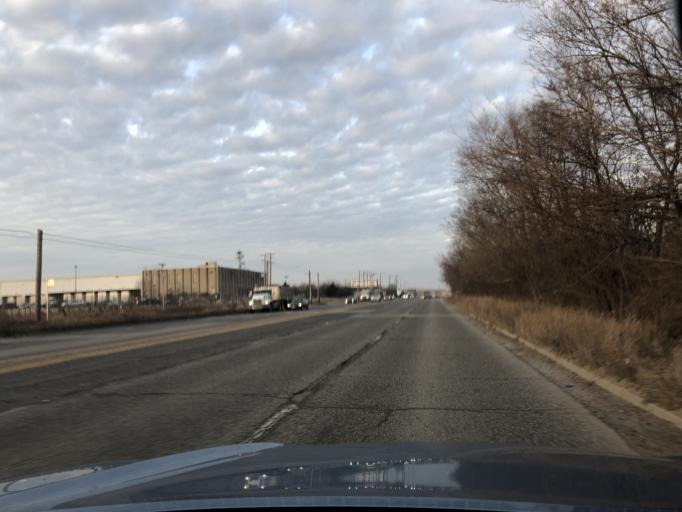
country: US
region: Illinois
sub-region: Cook County
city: Elk Grove Village
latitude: 42.0084
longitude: -87.9290
